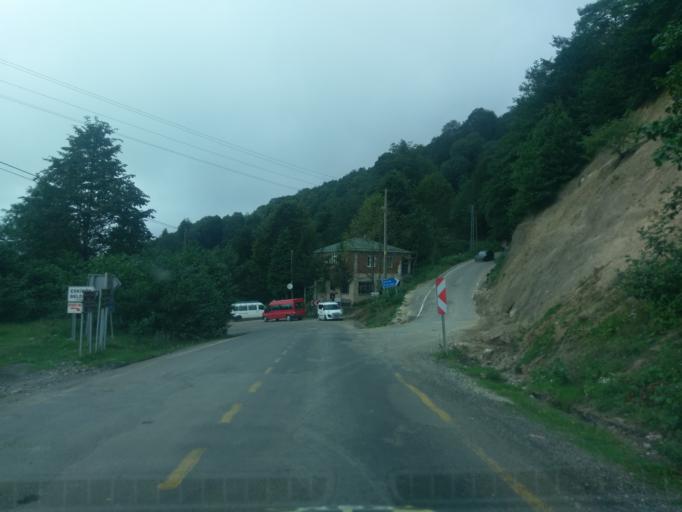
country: TR
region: Ordu
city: Gurgentepe
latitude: 40.8491
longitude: 37.6540
